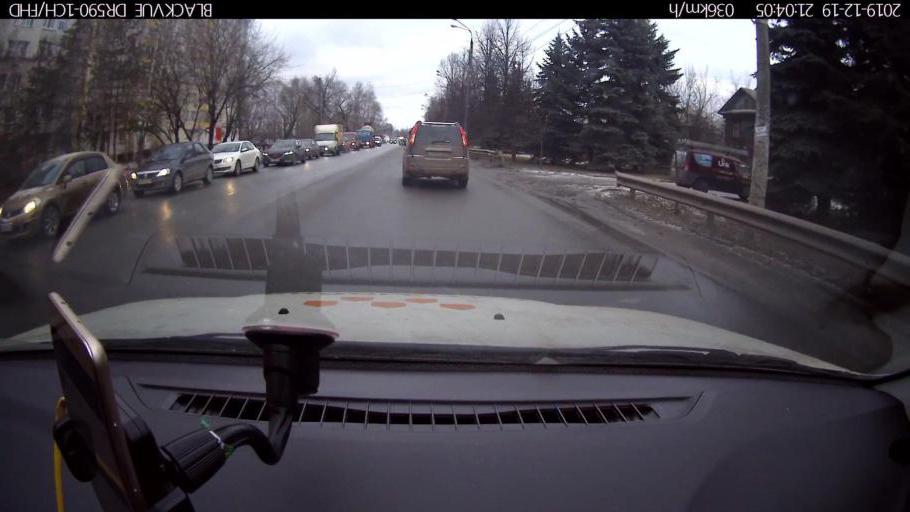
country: RU
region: Nizjnij Novgorod
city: Gorbatovka
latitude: 56.3454
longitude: 43.8397
